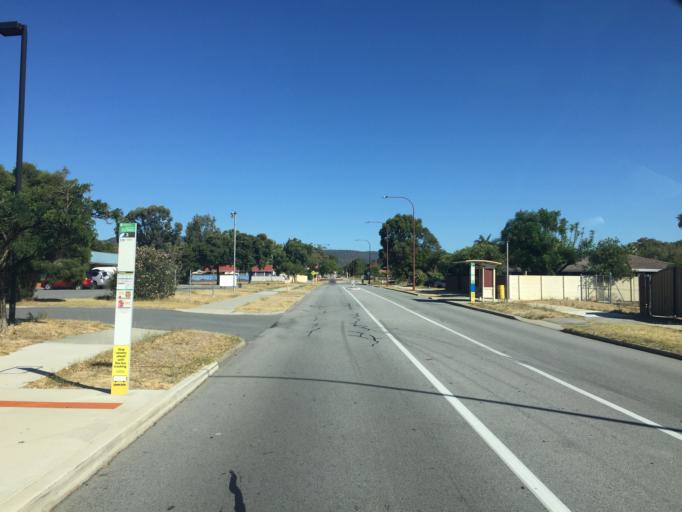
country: AU
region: Western Australia
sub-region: Gosnells
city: Maddington
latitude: -32.0541
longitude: 116.0010
